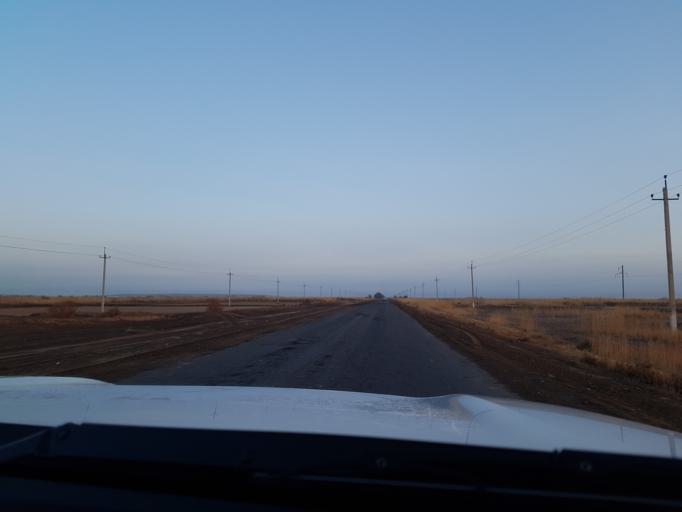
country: TM
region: Dasoguz
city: Koeneuergench
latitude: 41.7513
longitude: 58.6897
